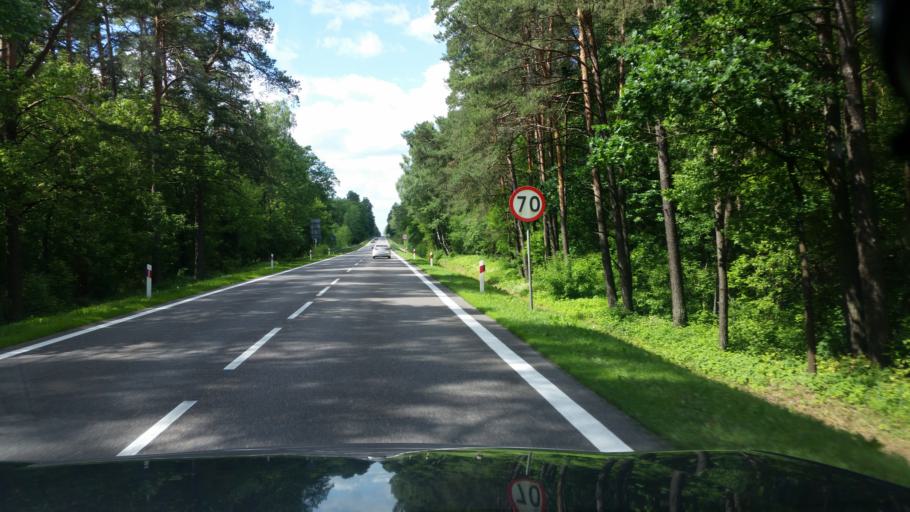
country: PL
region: Podlasie
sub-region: Powiat grajewski
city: Rajgrod
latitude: 53.6997
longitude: 22.6539
